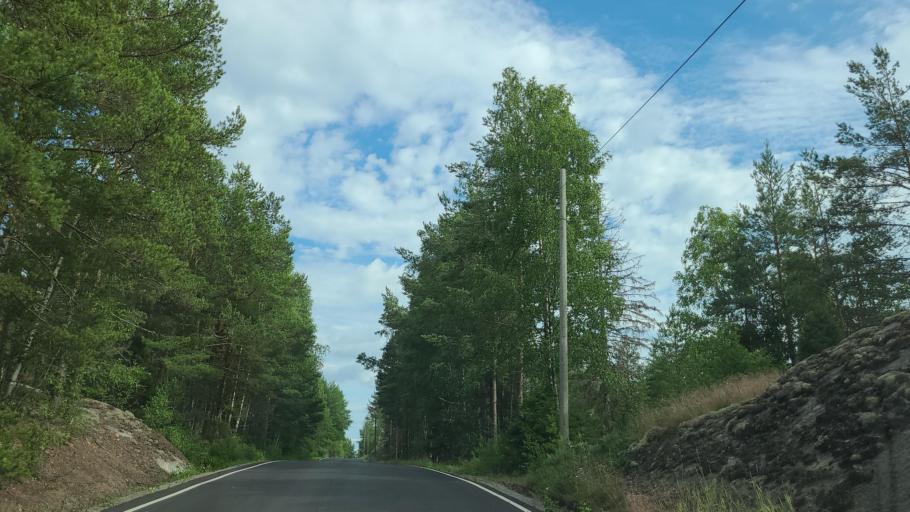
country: FI
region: Varsinais-Suomi
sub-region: Turku
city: Rymaettylae
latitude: 60.3205
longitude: 21.9576
